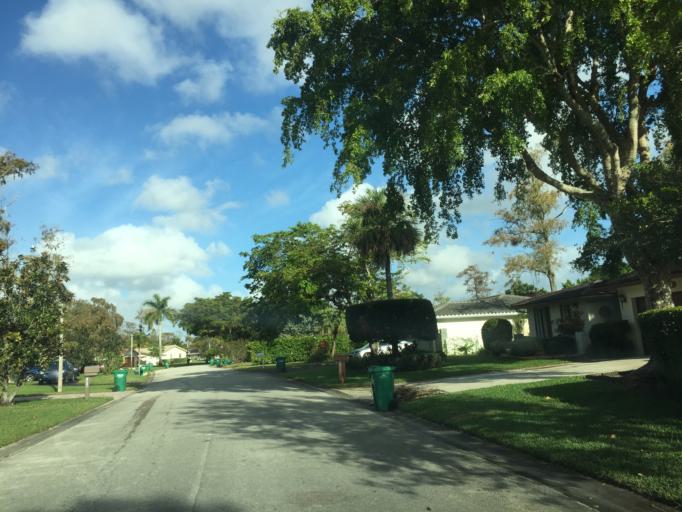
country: US
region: Florida
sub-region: Broward County
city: Margate
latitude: 26.2468
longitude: -80.2354
